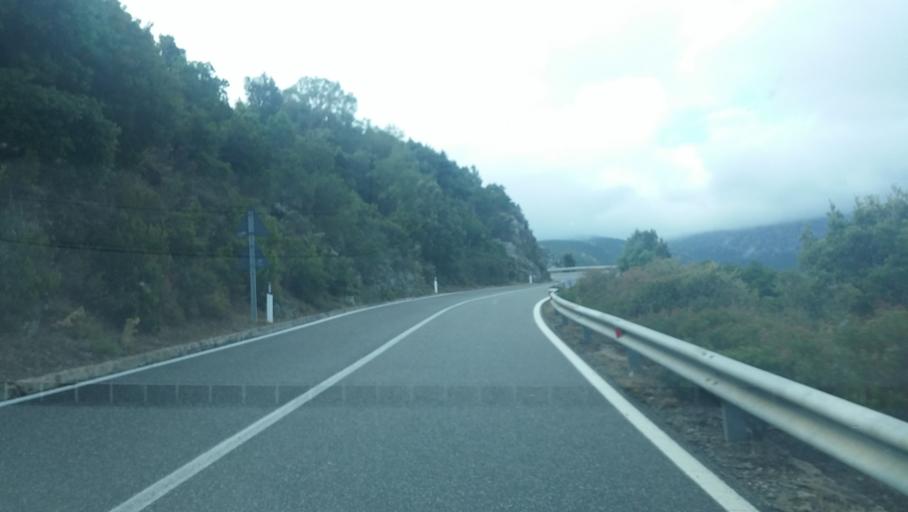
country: IT
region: Sardinia
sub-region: Provincia di Ogliastra
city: Urzulei
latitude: 40.1880
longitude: 9.5360
